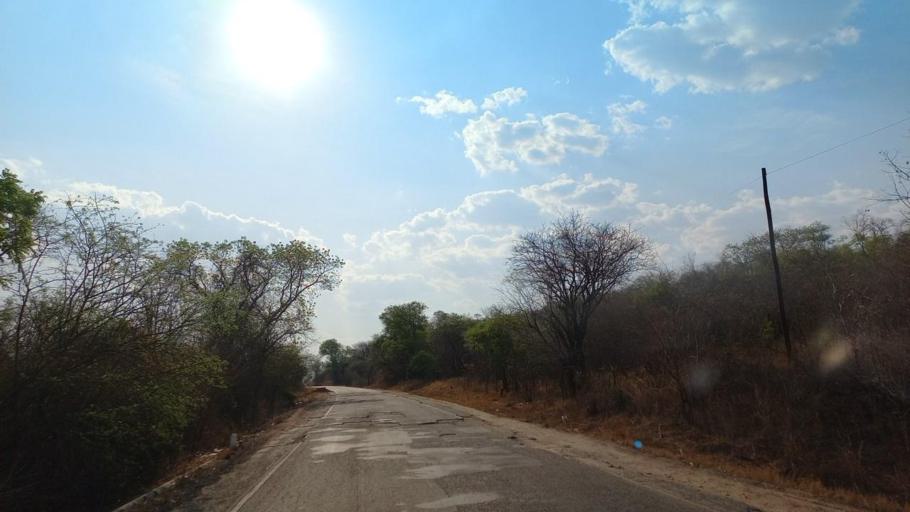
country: ZM
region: Lusaka
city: Luangwa
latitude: -14.9828
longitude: 30.1639
